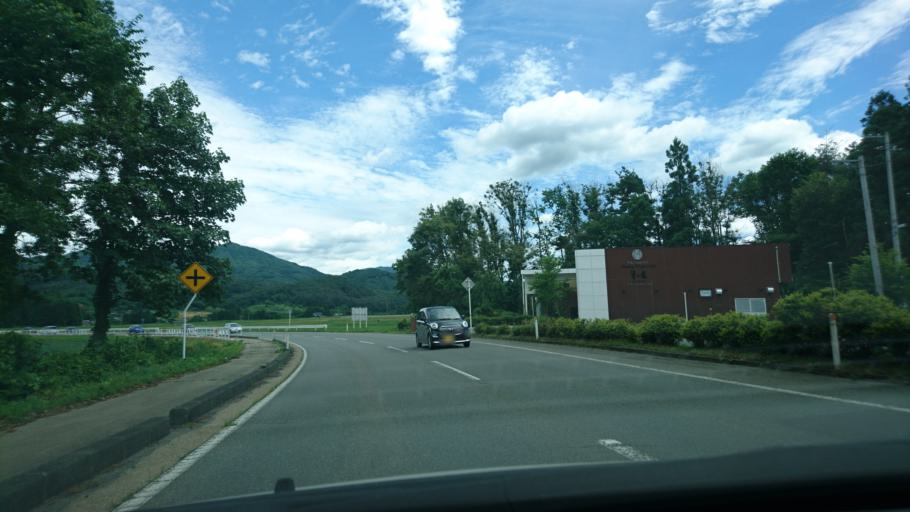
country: JP
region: Iwate
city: Morioka-shi
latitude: 39.6017
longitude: 141.2043
